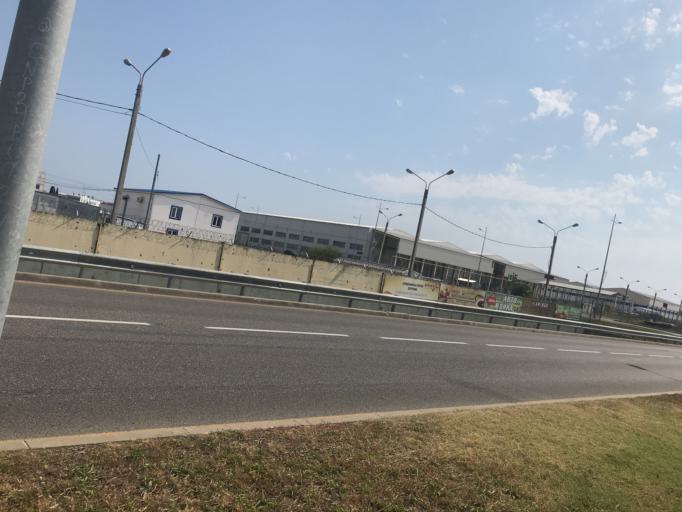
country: RU
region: Krasnodarskiy
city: Vysokoye
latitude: 43.3990
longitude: 39.9837
